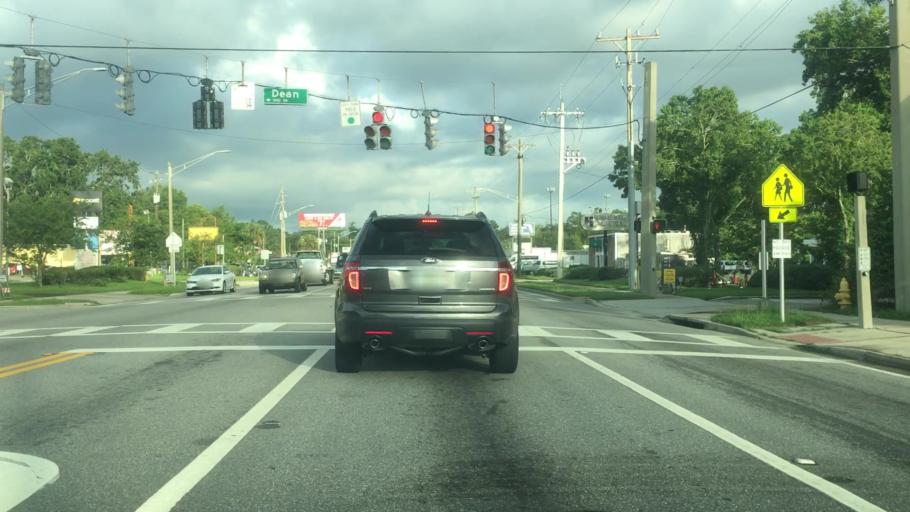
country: US
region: Florida
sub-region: Duval County
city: Jacksonville
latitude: 30.2686
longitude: -81.5770
